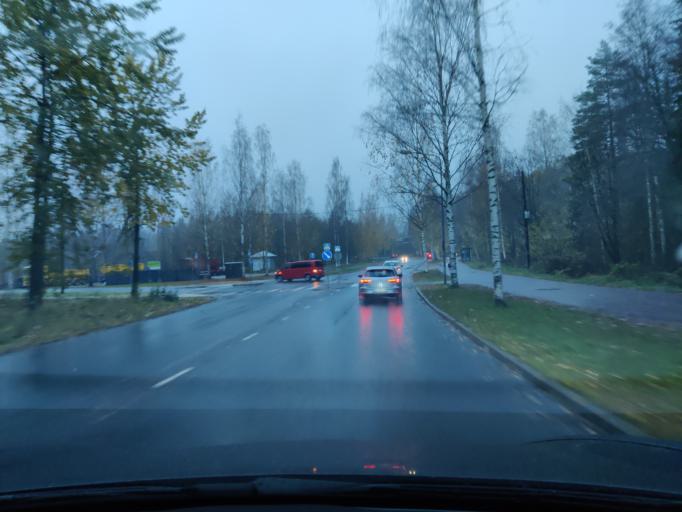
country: FI
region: Northern Savo
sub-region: Kuopio
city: Kuopio
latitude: 62.8496
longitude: 27.6407
